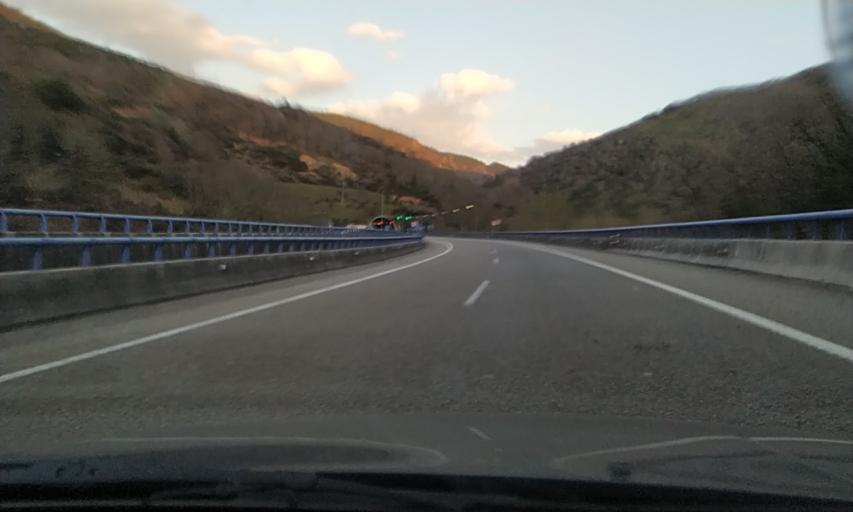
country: ES
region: Castille and Leon
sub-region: Provincia de Leon
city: Trabadelo
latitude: 42.6403
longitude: -6.8684
